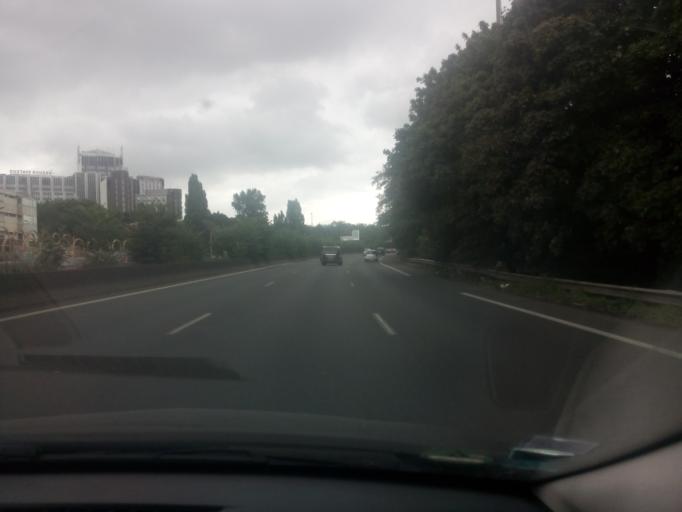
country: FR
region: Ile-de-France
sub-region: Departement du Val-de-Marne
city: Cachan
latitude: 48.7968
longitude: 2.3441
